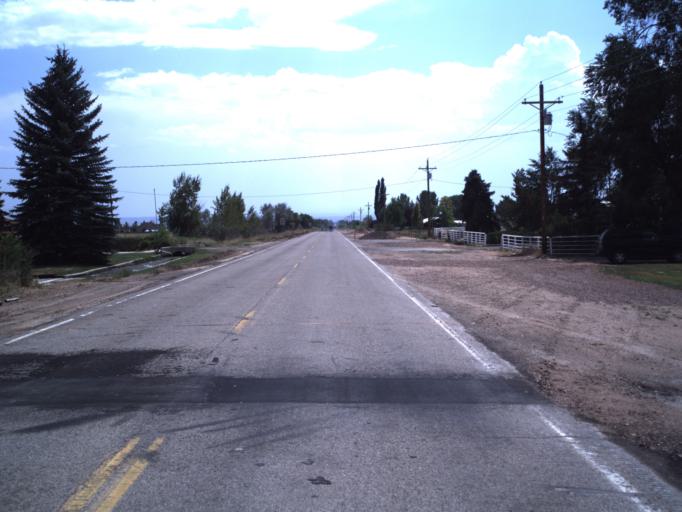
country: US
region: Utah
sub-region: Duchesne County
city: Roosevelt
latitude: 40.4264
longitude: -110.0301
